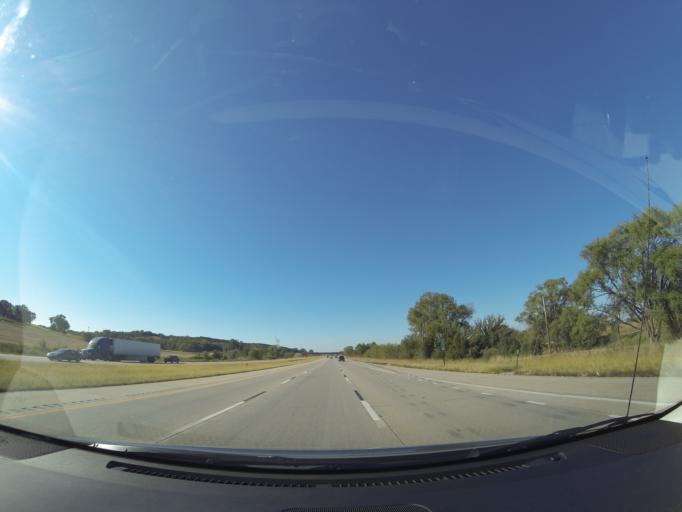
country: US
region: Nebraska
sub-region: Sarpy County
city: Gretna
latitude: 41.0770
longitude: -96.2815
